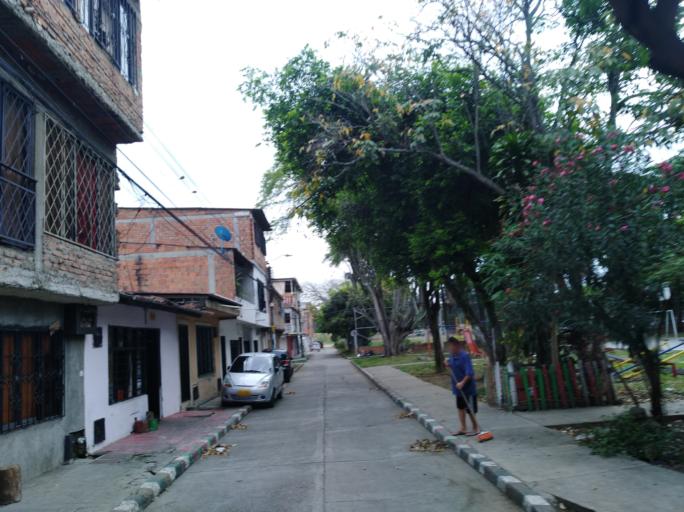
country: CO
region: Valle del Cauca
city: Cali
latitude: 3.4820
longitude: -76.4835
